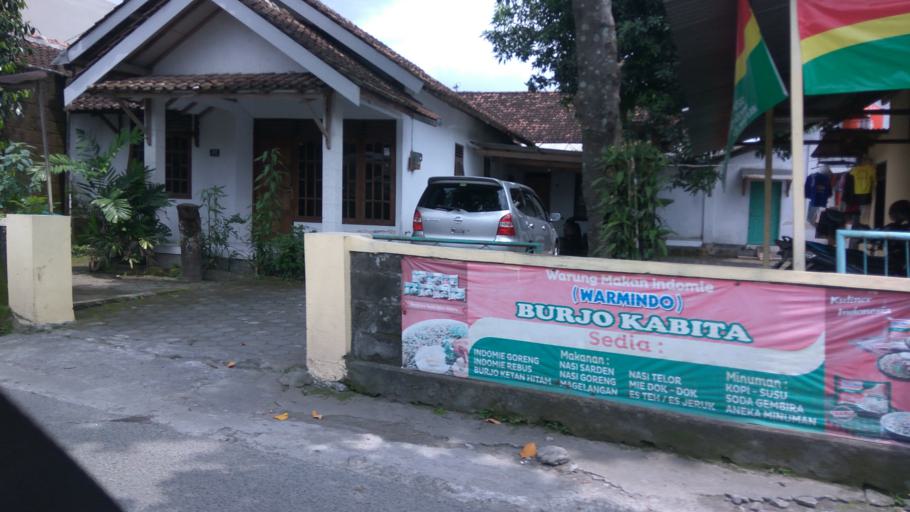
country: ID
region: Daerah Istimewa Yogyakarta
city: Depok
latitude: -7.7505
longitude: 110.4094
